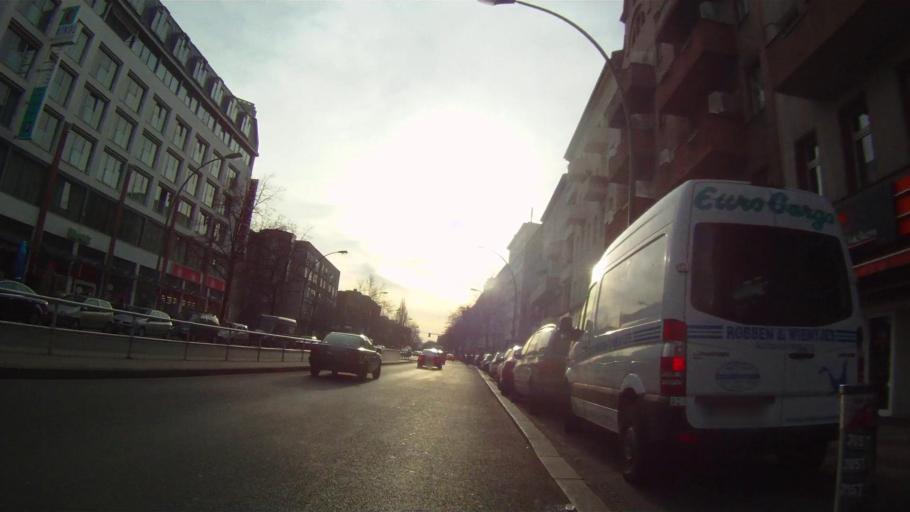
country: DE
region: Berlin
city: Berlin Treptow
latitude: 52.4788
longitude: 13.4256
